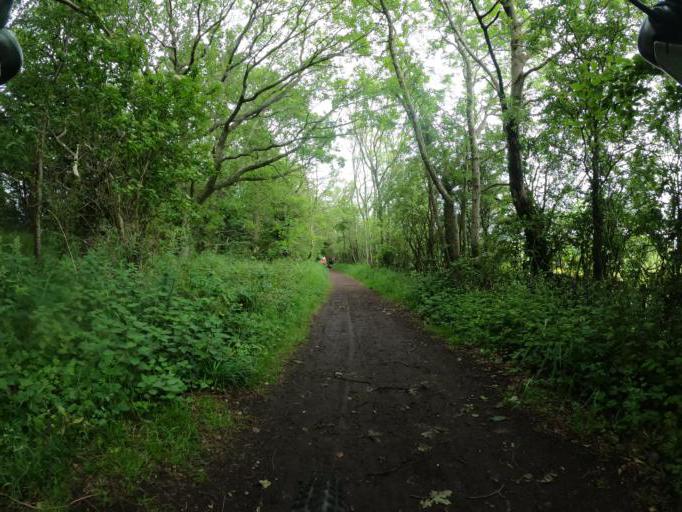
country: GB
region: Scotland
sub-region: Edinburgh
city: Currie
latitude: 55.9074
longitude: -3.3043
